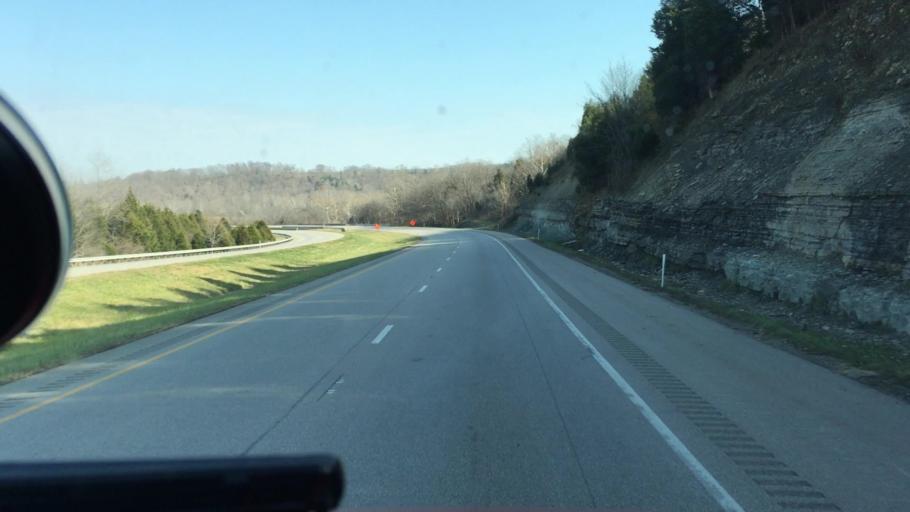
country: US
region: Kentucky
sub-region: Bath County
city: Owingsville
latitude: 38.1111
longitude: -83.8101
